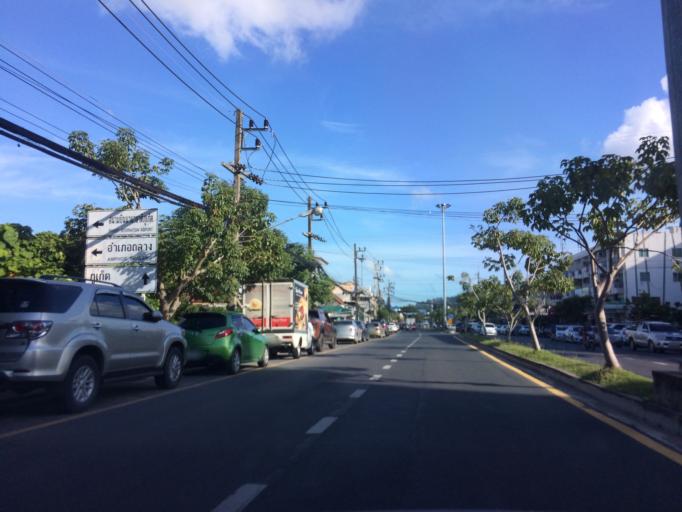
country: TH
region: Phuket
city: Kathu
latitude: 7.9101
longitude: 98.3474
